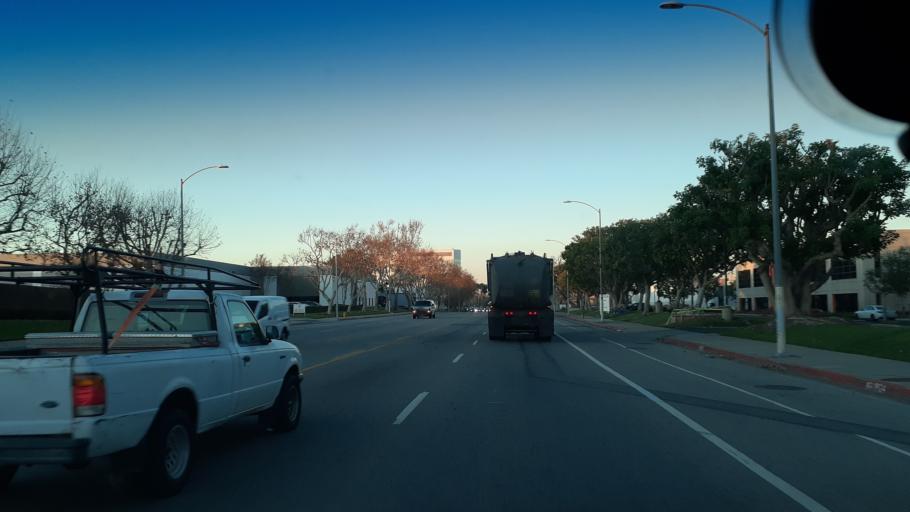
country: US
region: California
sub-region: Los Angeles County
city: Carson
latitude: 33.8509
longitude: -118.2905
